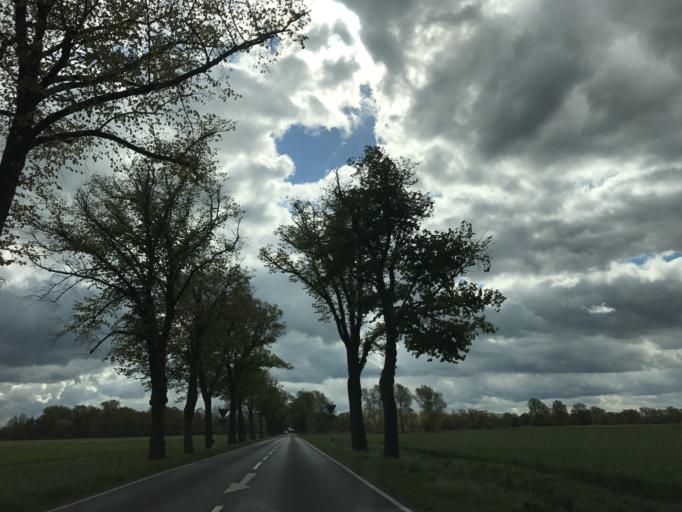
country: DE
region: Brandenburg
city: Roskow
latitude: 52.4792
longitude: 12.6986
